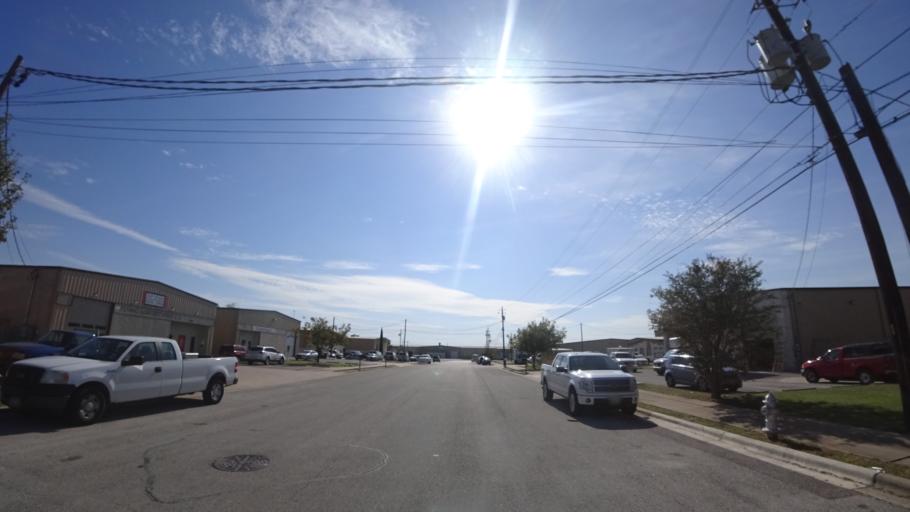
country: US
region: Texas
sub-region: Travis County
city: Pflugerville
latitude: 30.4025
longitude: -97.6286
